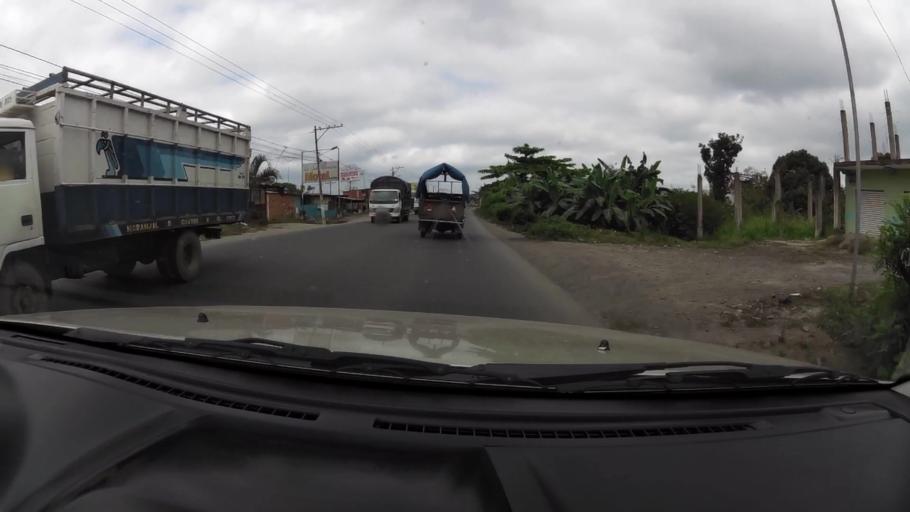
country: EC
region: Guayas
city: Naranjal
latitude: -2.6825
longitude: -79.6224
